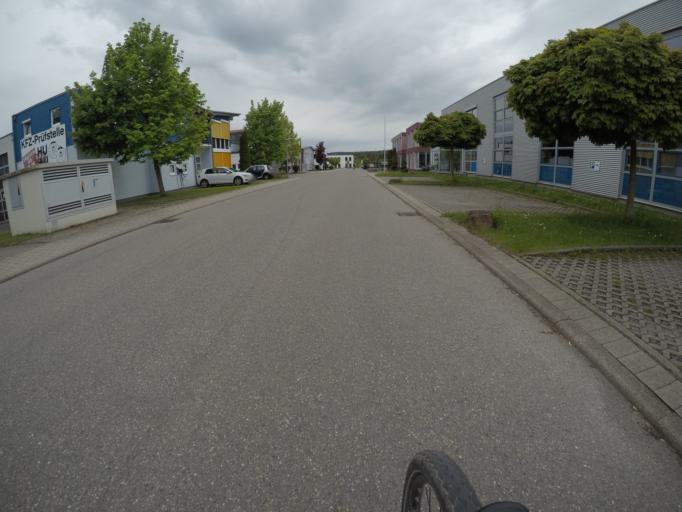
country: DE
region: Baden-Wuerttemberg
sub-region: Regierungsbezirk Stuttgart
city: Gartringen
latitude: 48.6323
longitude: 8.9000
